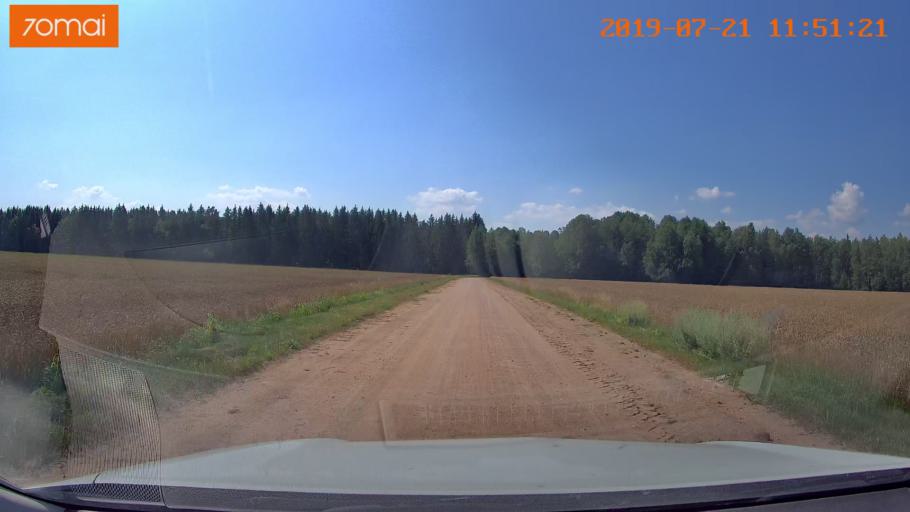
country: BY
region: Grodnenskaya
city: Lyubcha
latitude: 53.8841
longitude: 26.0132
